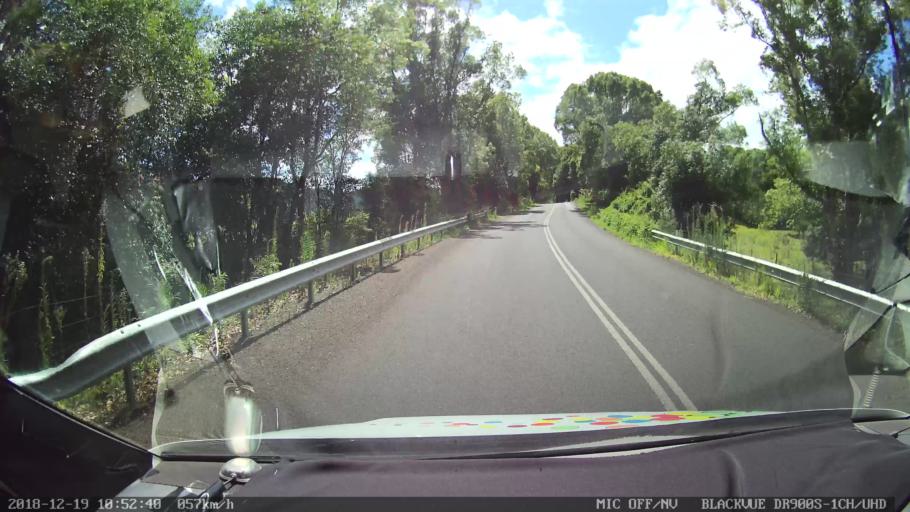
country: AU
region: New South Wales
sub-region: Lismore Municipality
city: Nimbin
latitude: -28.5912
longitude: 153.2318
